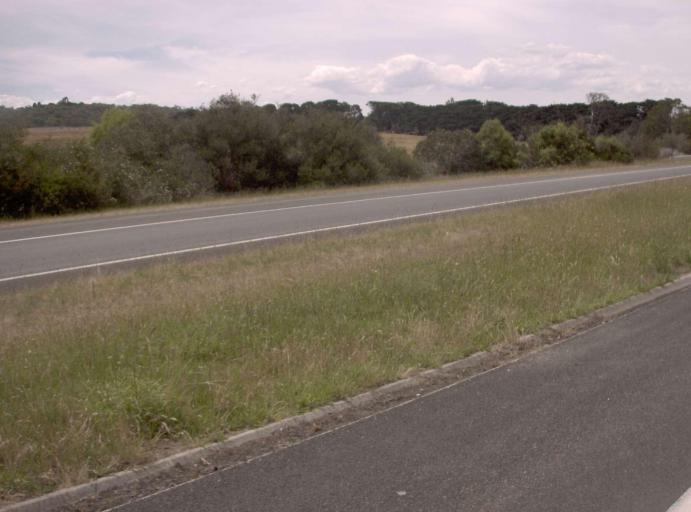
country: AU
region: Victoria
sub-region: Mornington Peninsula
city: Safety Beach
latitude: -38.3031
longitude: 145.0280
